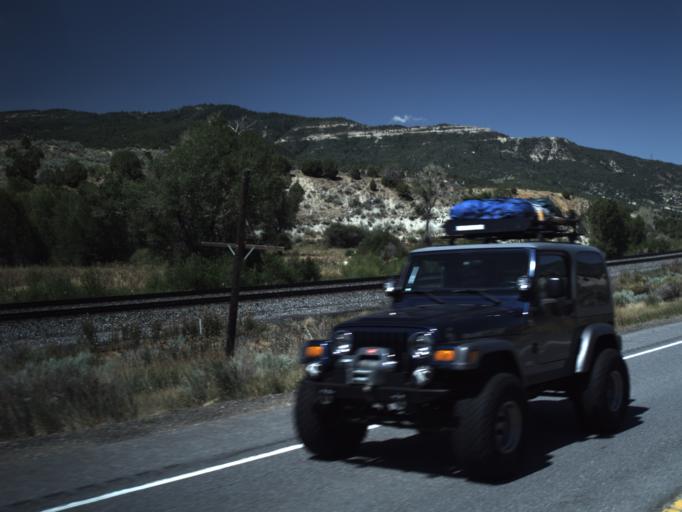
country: US
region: Utah
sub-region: Utah County
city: Mapleton
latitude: 39.9670
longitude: -111.3224
